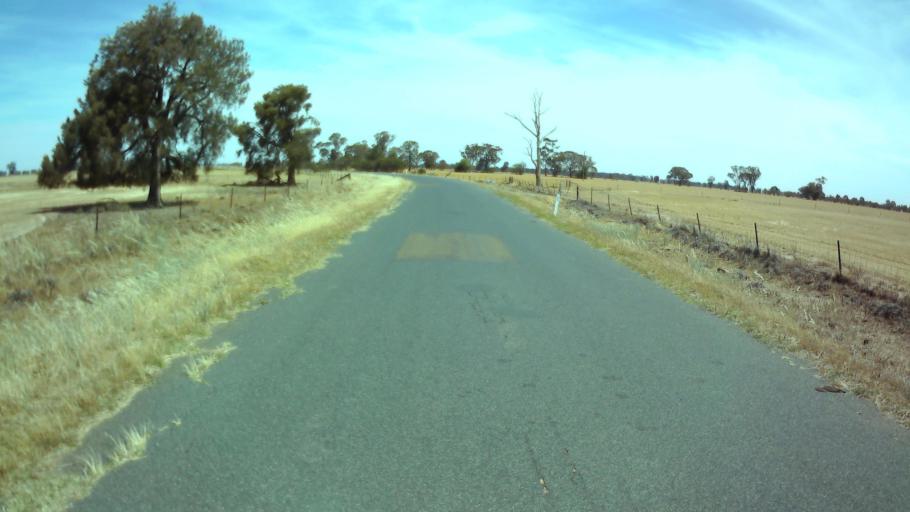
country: AU
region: New South Wales
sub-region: Weddin
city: Grenfell
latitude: -33.9354
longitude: 147.7615
